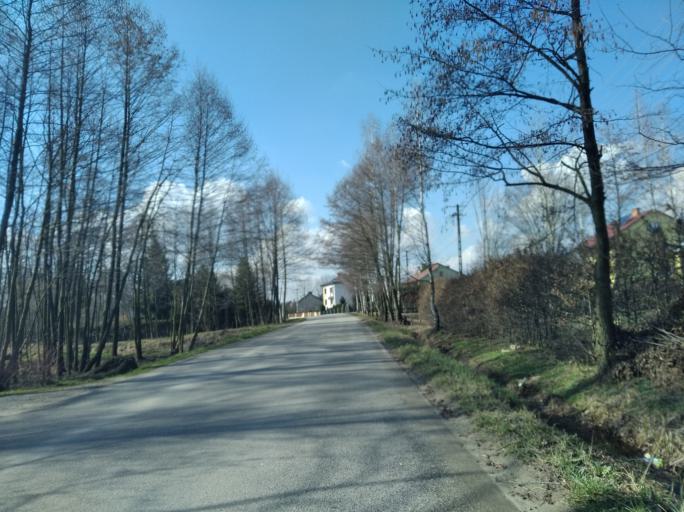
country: PL
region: Subcarpathian Voivodeship
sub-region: Powiat debicki
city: Brzostek
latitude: 49.8816
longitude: 21.4248
